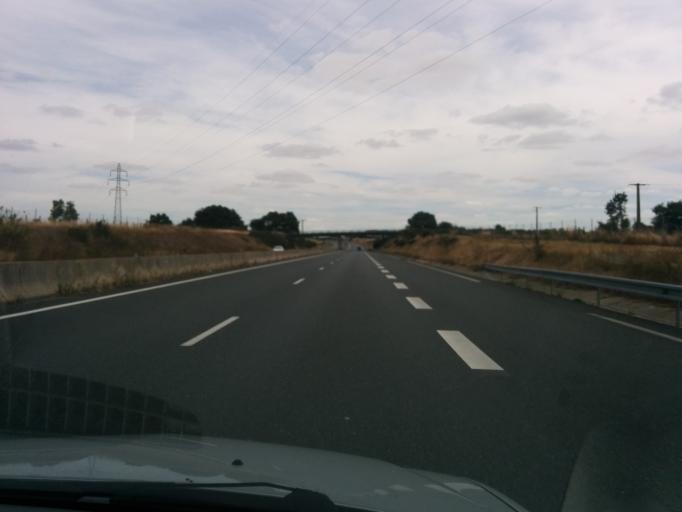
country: FR
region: Poitou-Charentes
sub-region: Departement des Deux-Sevres
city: Saint-Pierre-des-Echaubrognes
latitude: 46.9385
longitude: -0.7495
